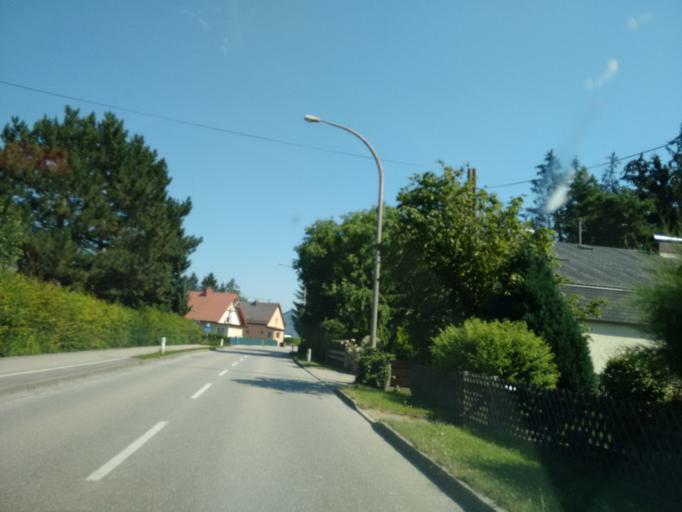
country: AT
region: Upper Austria
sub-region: Politischer Bezirk Urfahr-Umgebung
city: Feldkirchen an der Donau
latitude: 48.3161
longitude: 14.0176
